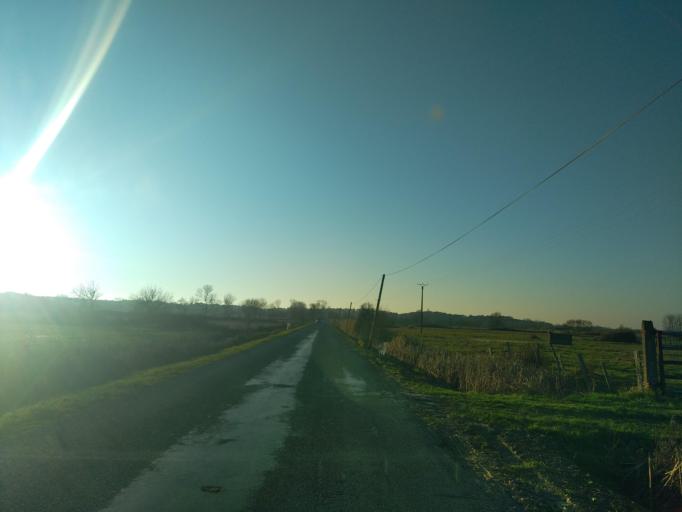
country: FR
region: Pays de la Loire
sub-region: Departement de la Vendee
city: La Tranche-sur-Mer
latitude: 46.3878
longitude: -1.4546
